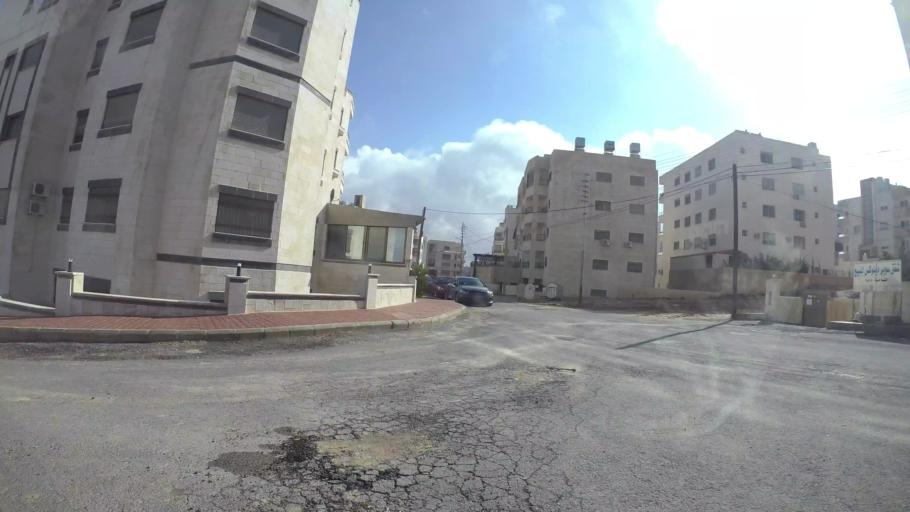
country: JO
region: Amman
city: Al Jubayhah
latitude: 32.0416
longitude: 35.8744
